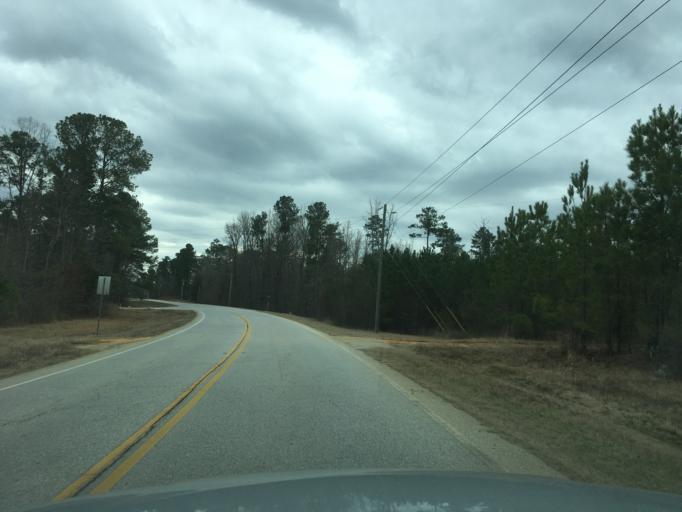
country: US
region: Georgia
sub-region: Lincoln County
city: Lincolnton
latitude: 33.8351
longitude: -82.4104
